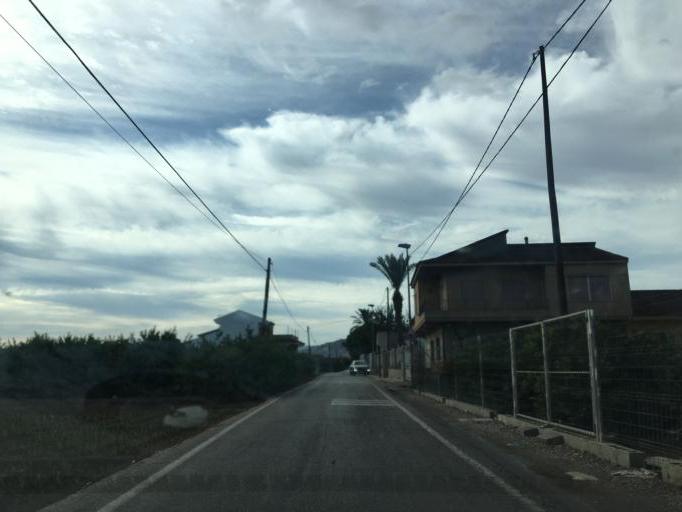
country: ES
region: Murcia
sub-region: Murcia
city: Santomera
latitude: 38.0187
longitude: -1.0483
